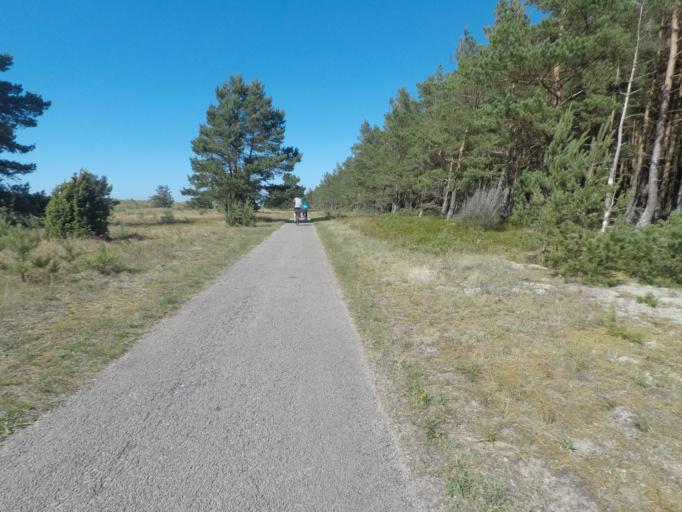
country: LT
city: Neringa
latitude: 55.5003
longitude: 21.0896
